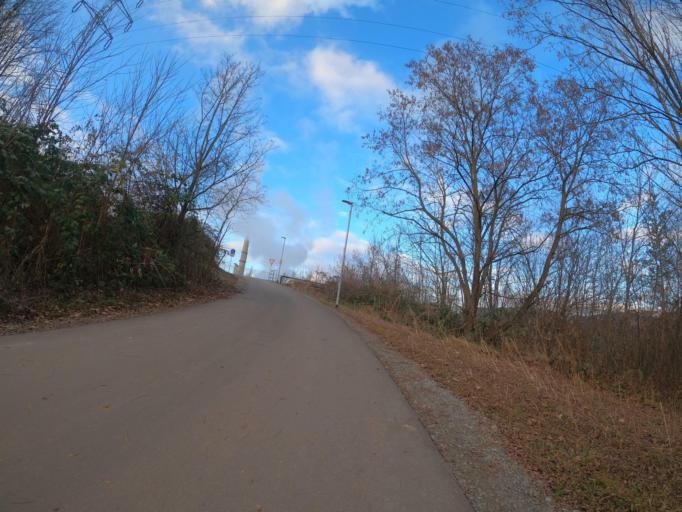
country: DE
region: Thuringia
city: Jena
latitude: 50.8935
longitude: 11.5897
